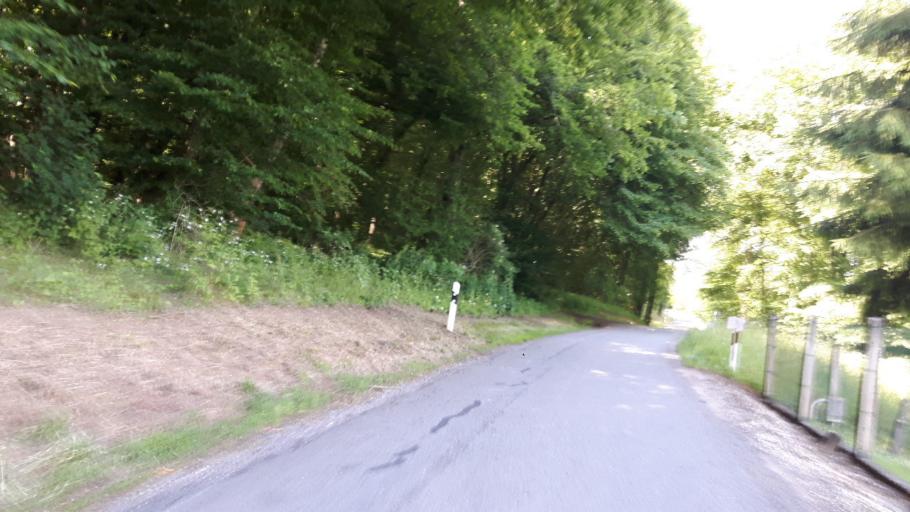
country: DE
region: Thuringia
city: Wichmar
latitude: 51.0323
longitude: 11.6820
